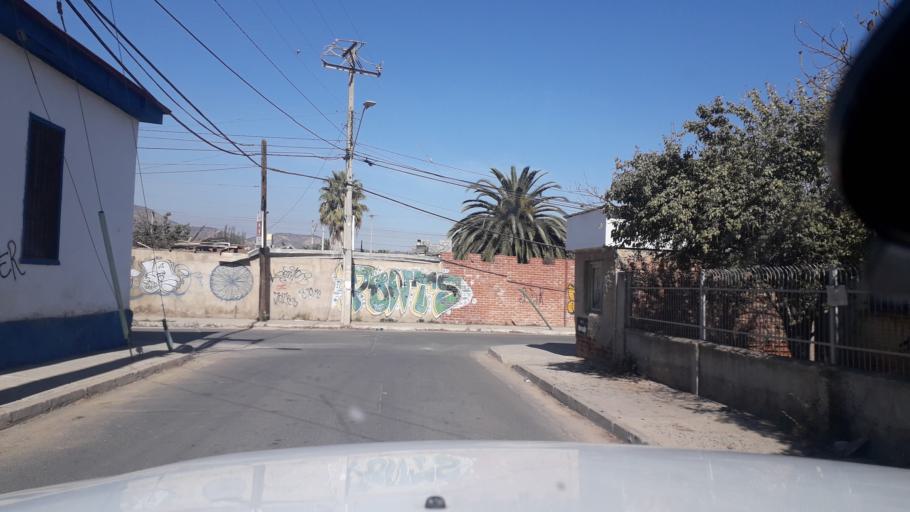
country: CL
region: Valparaiso
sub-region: Provincia de Marga Marga
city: Villa Alemana
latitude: -33.0398
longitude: -71.3550
